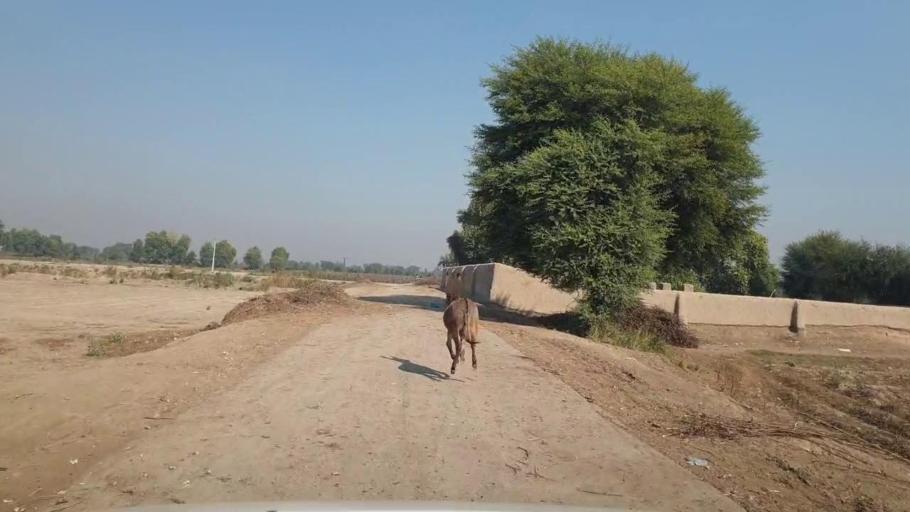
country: PK
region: Sindh
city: Bhan
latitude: 26.6152
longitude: 67.7607
